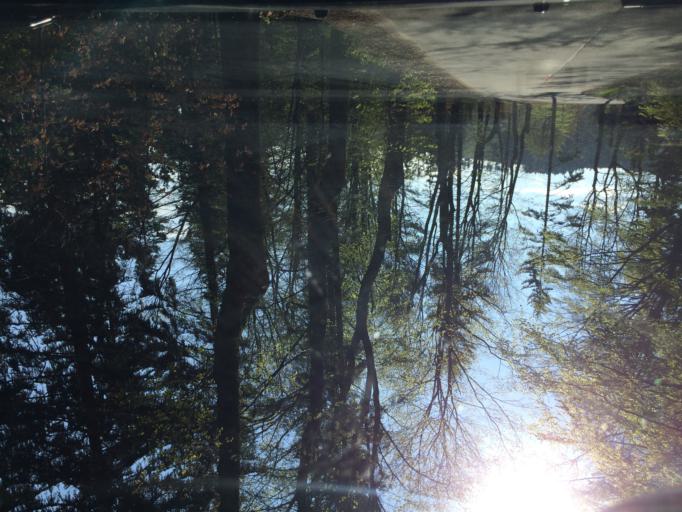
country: PL
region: Lower Silesian Voivodeship
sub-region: Powiat klodzki
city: Jugow
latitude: 50.6534
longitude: 16.5173
